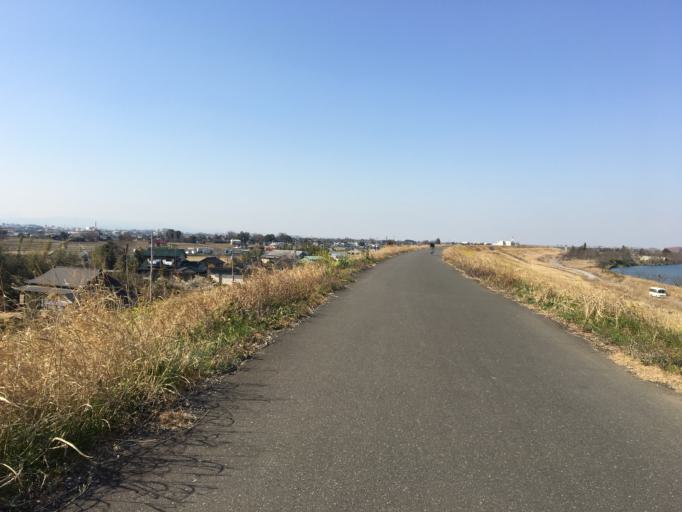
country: JP
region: Saitama
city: Shiki
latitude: 35.8616
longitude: 139.5797
